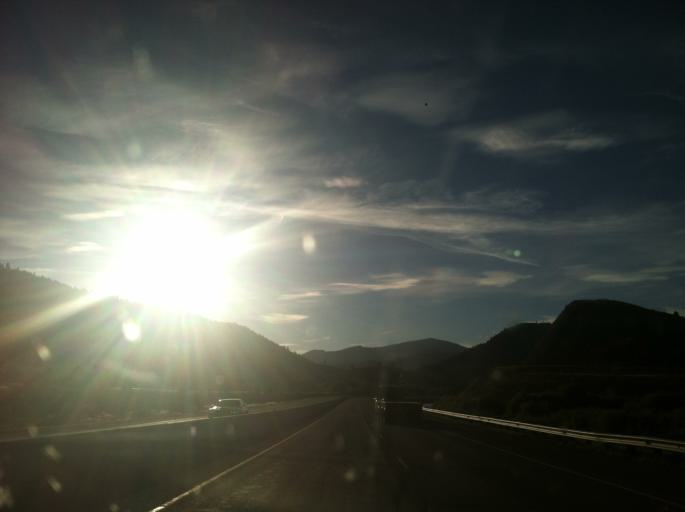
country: US
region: Montana
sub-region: Granite County
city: Philipsburg
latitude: 46.7134
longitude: -113.2761
